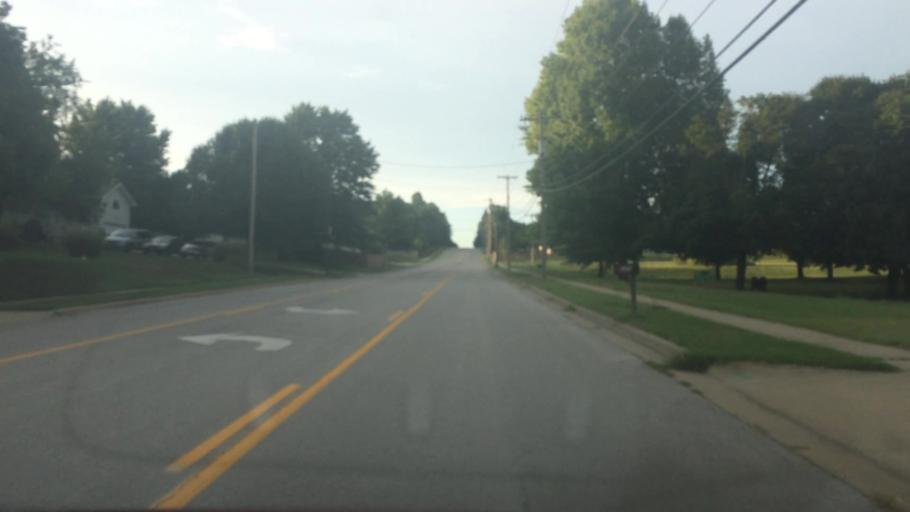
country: US
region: Missouri
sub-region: Greene County
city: Strafford
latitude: 37.1997
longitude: -93.1889
